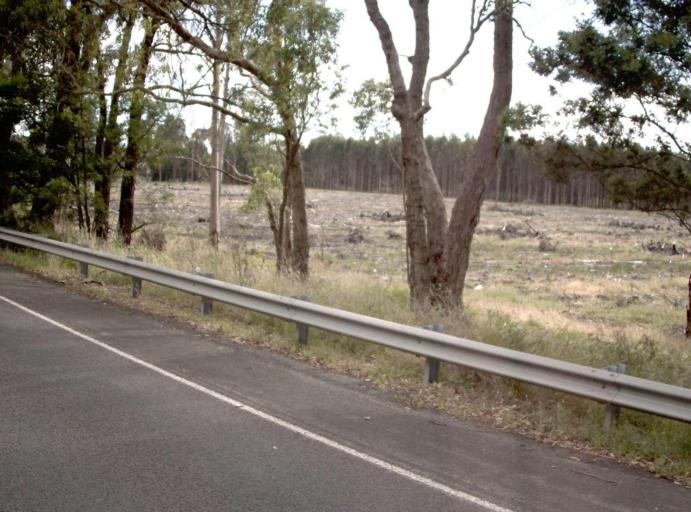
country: AU
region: Victoria
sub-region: Latrobe
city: Morwell
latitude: -38.1958
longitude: 146.4379
